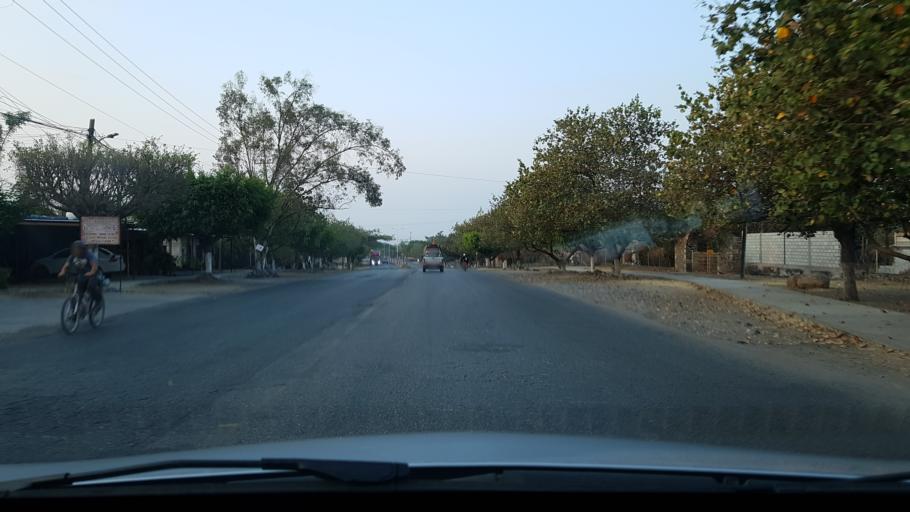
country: MX
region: Morelos
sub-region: Jonacatepec
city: Amacuitlapilco
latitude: 18.6999
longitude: -98.8013
